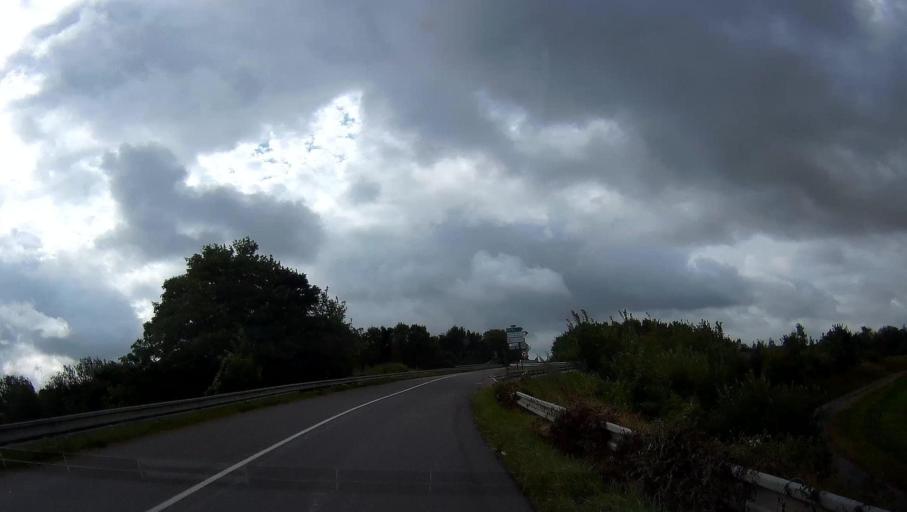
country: FR
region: Champagne-Ardenne
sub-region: Departement des Ardennes
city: Rethel
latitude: 49.5203
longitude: 4.3509
